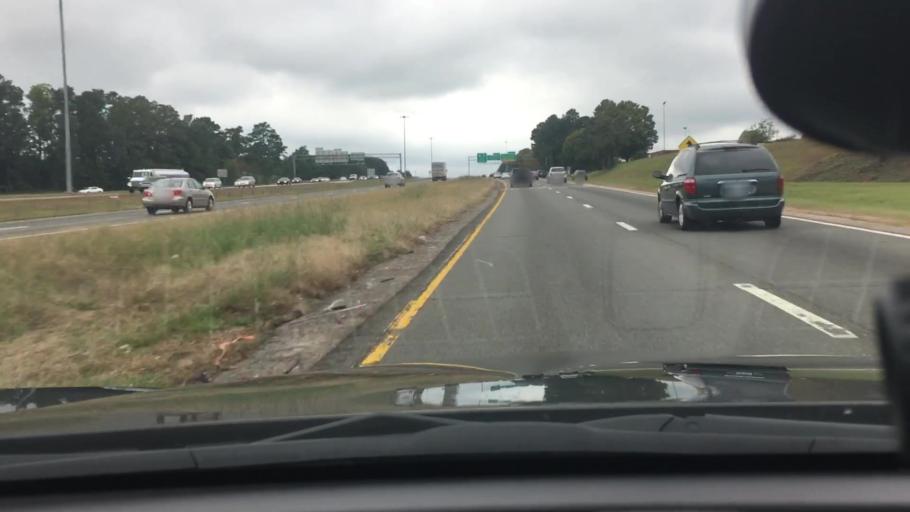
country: US
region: North Carolina
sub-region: Wake County
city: Cary
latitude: 35.7662
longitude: -78.7374
